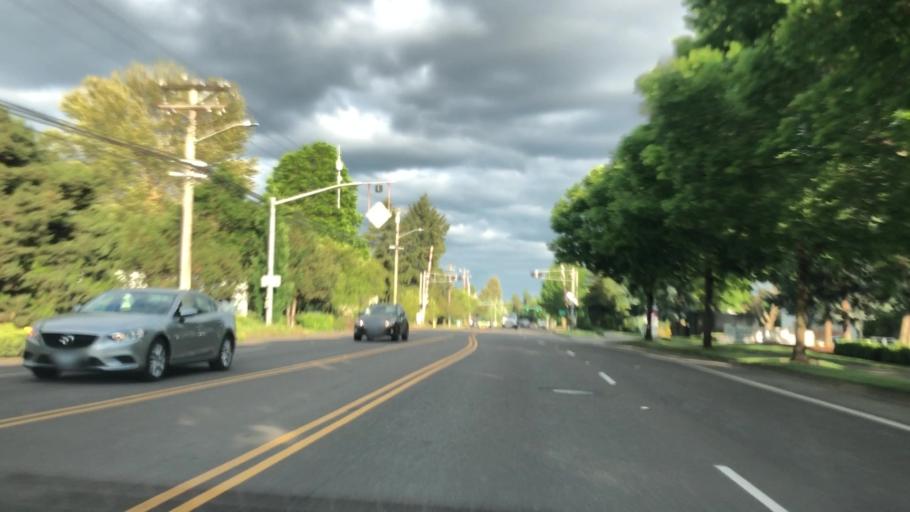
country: US
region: Oregon
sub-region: Washington County
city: Raleigh Hills
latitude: 45.4761
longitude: -122.7815
